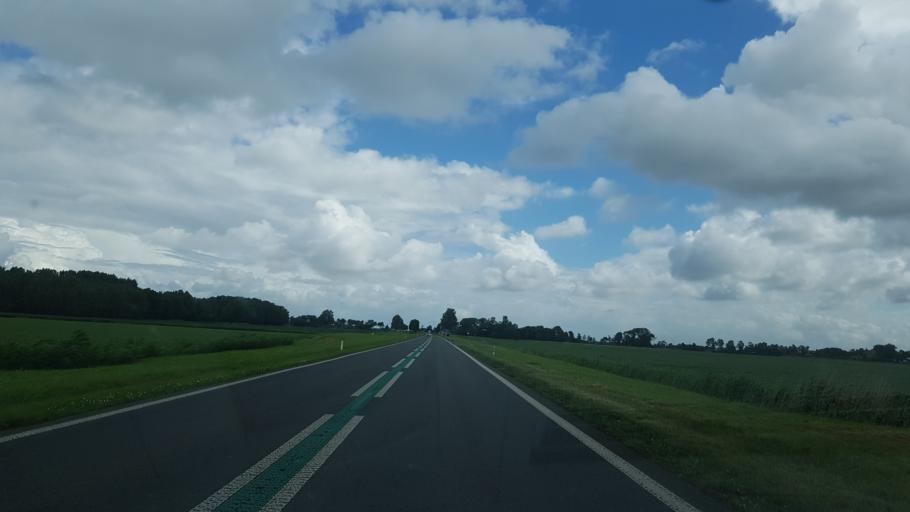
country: NL
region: Friesland
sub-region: Gemeente Dongeradeel
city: Anjum
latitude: 53.3535
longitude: 6.0687
